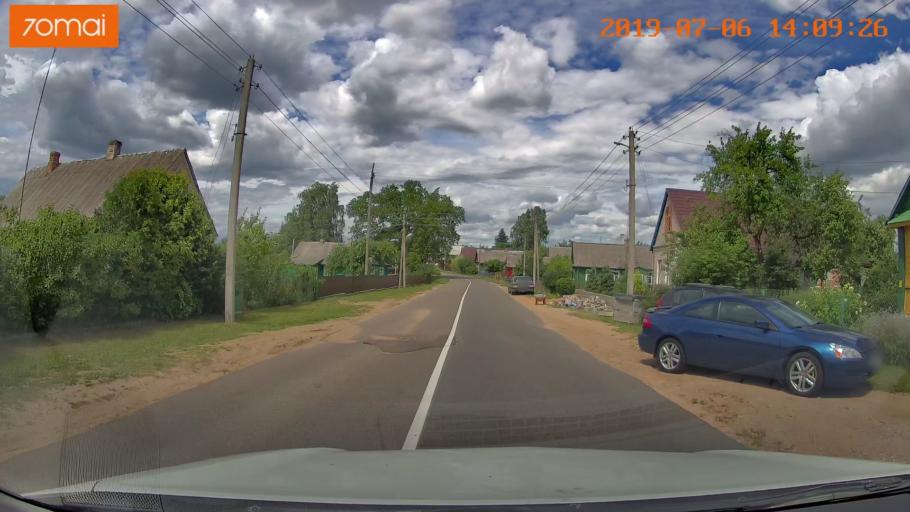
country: BY
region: Minsk
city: Ivyanyets
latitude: 53.8817
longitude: 26.7486
